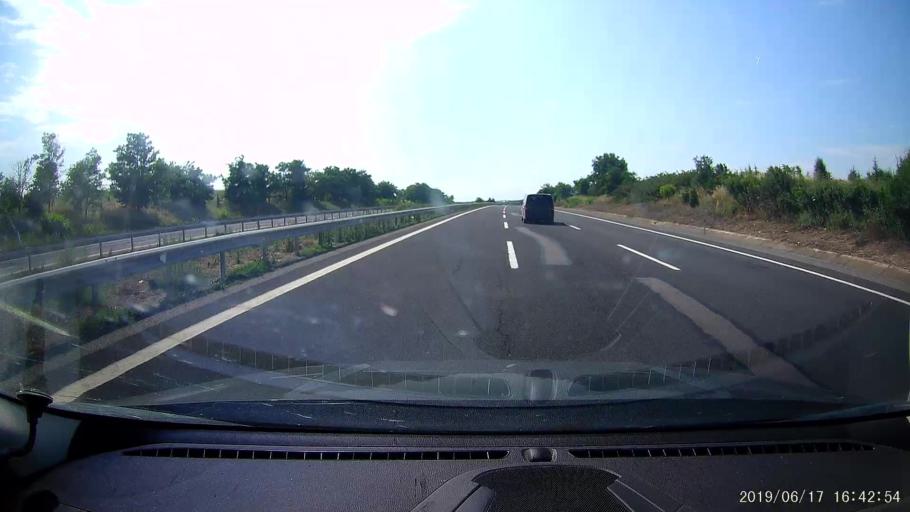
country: TR
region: Kirklareli
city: Luleburgaz
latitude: 41.4765
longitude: 27.3093
